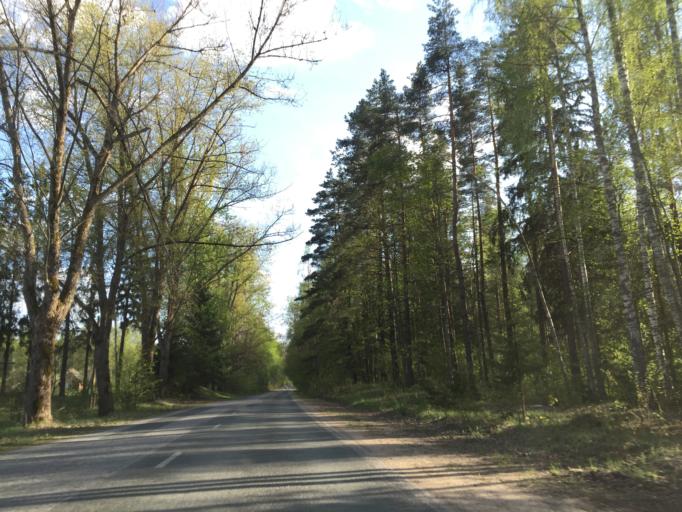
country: LV
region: Sigulda
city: Sigulda
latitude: 57.1979
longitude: 24.8495
